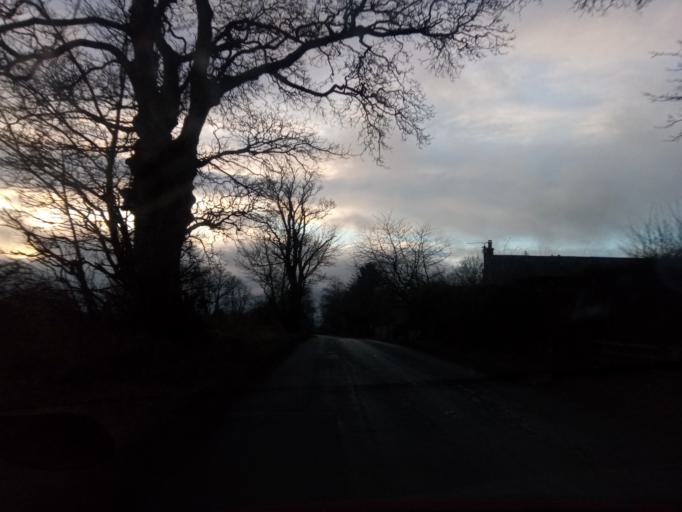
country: GB
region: England
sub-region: Northumberland
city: Meldon
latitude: 55.1315
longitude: -1.7895
